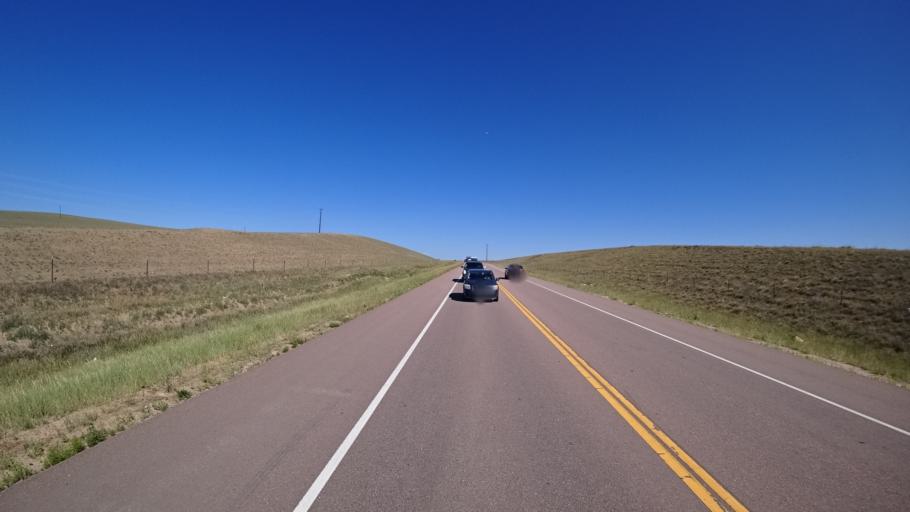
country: US
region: Colorado
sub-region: El Paso County
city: Cimarron Hills
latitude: 38.7998
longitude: -104.6610
